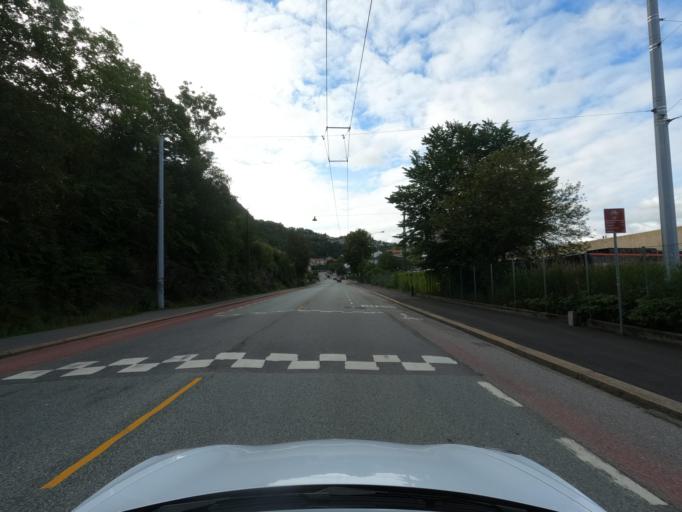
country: NO
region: Hordaland
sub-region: Bergen
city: Bergen
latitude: 60.3557
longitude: 5.3683
